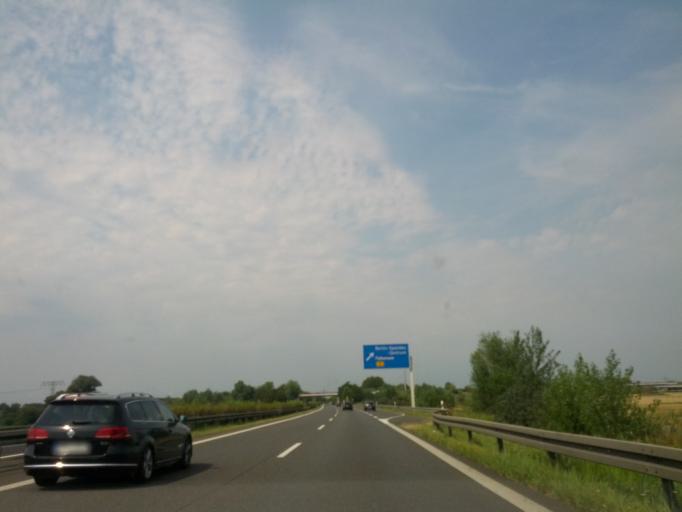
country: DE
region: Brandenburg
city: Wustermark
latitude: 52.5361
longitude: 12.9661
